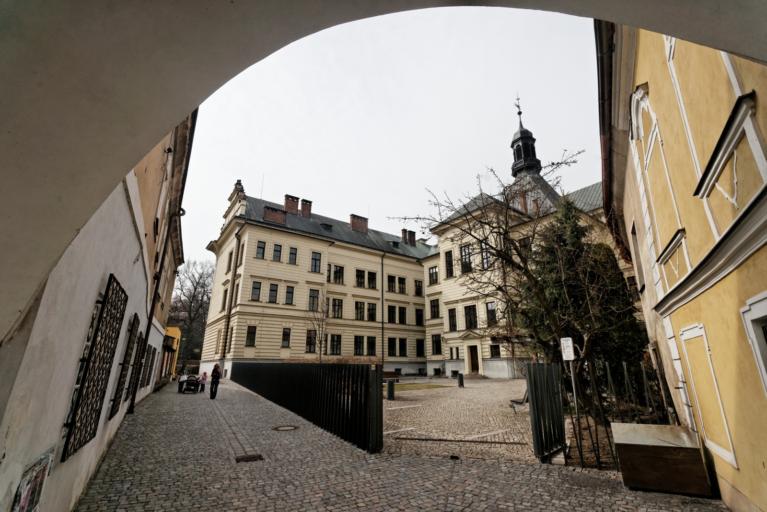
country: CZ
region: Pardubicky
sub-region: Okres Svitavy
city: Litomysl
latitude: 49.8728
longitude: 16.3096
